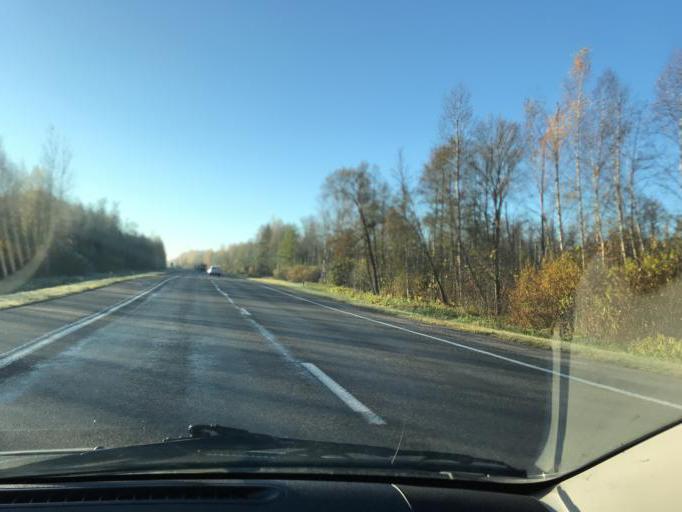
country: BY
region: Vitebsk
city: Vitebsk
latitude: 54.9595
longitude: 30.3565
